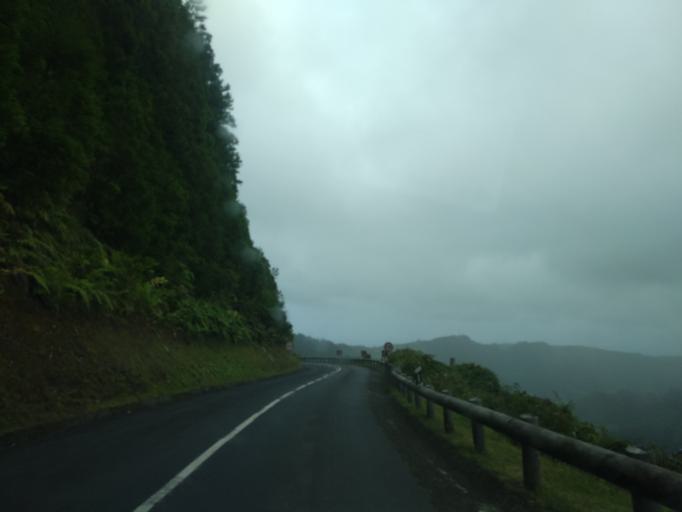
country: PT
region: Azores
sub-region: Ponta Delgada
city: Arrifes
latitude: 37.8386
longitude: -25.7890
